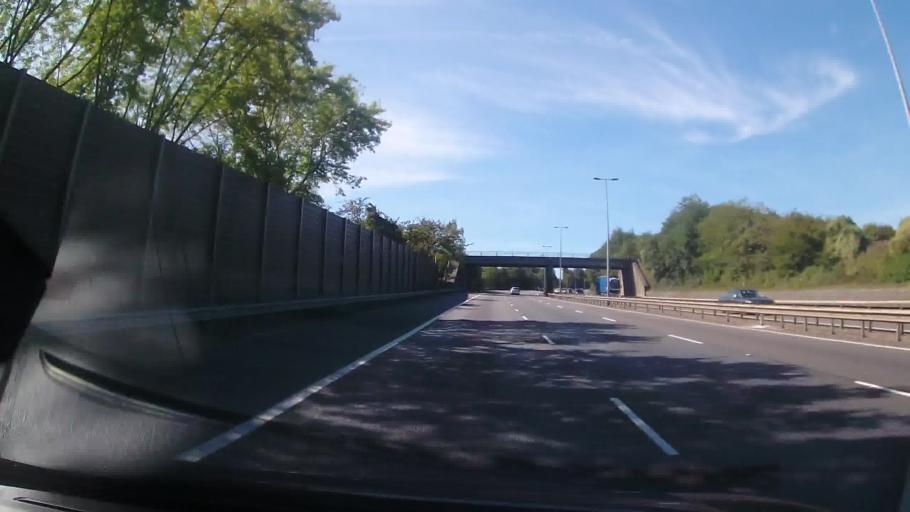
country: GB
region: England
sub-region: Buckinghamshire
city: Stokenchurch
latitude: 51.6249
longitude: -0.8335
